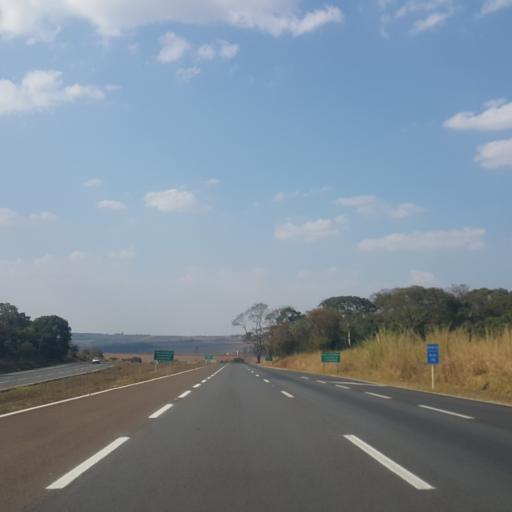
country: BR
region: Goias
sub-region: Abadiania
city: Abadiania
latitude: -16.2829
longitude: -48.7937
